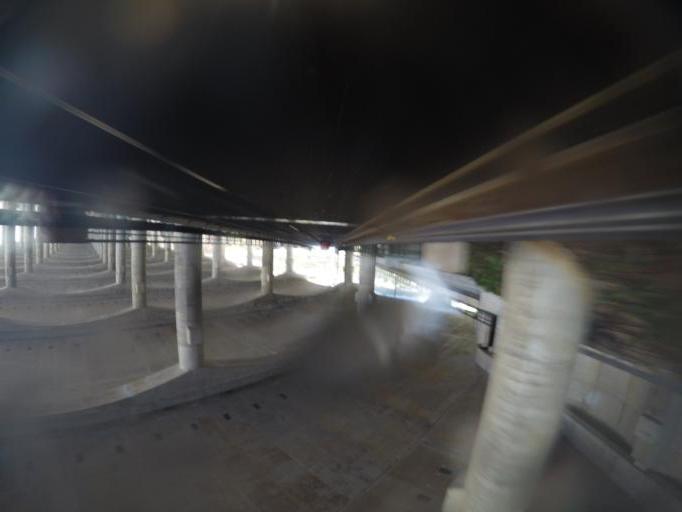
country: PT
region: Madeira
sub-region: Machico
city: Machico
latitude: 32.7010
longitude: -16.7710
